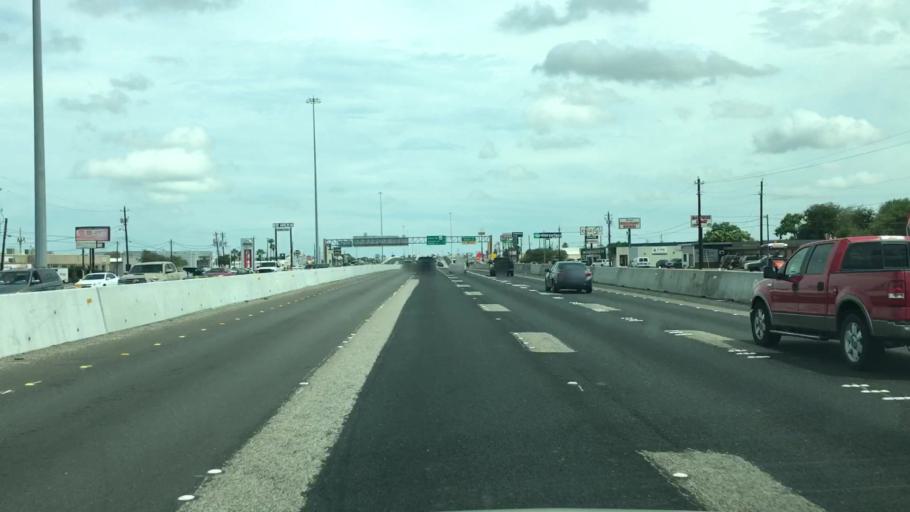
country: US
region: Texas
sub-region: Nueces County
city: Corpus Christi
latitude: 27.7315
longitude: -97.4191
